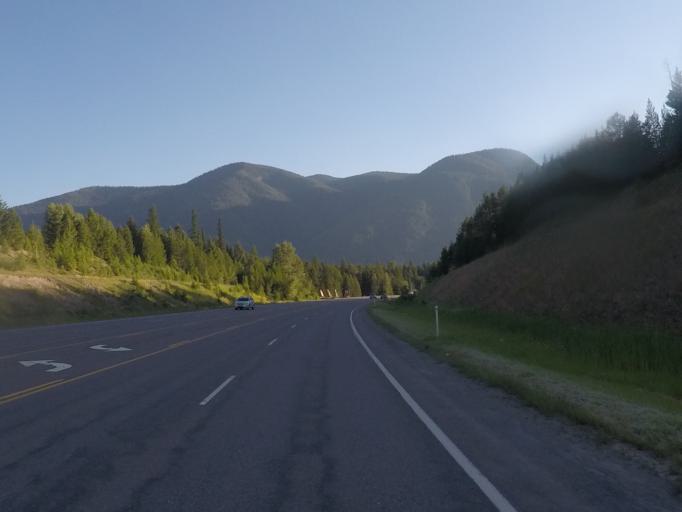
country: US
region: Montana
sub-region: Flathead County
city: Columbia Falls
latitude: 48.3895
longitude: -114.0434
